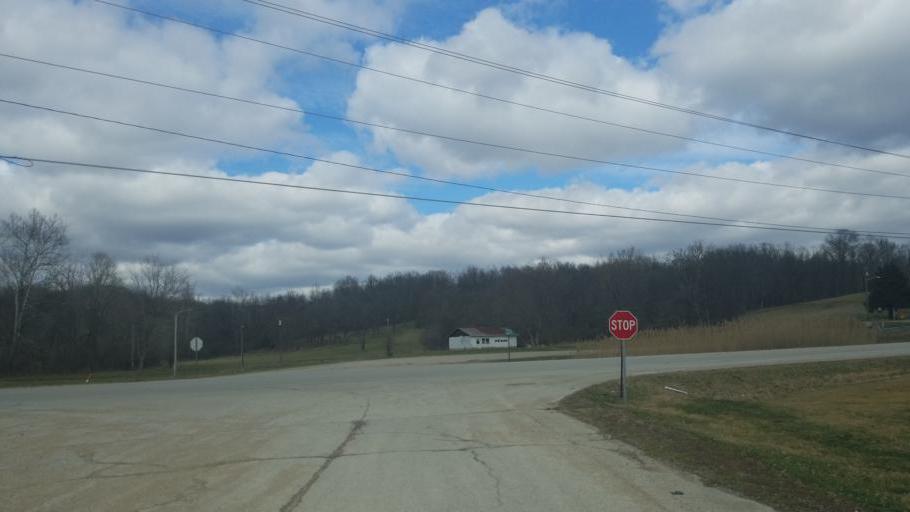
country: US
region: Indiana
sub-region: Parke County
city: Rockville
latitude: 39.7636
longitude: -87.2051
